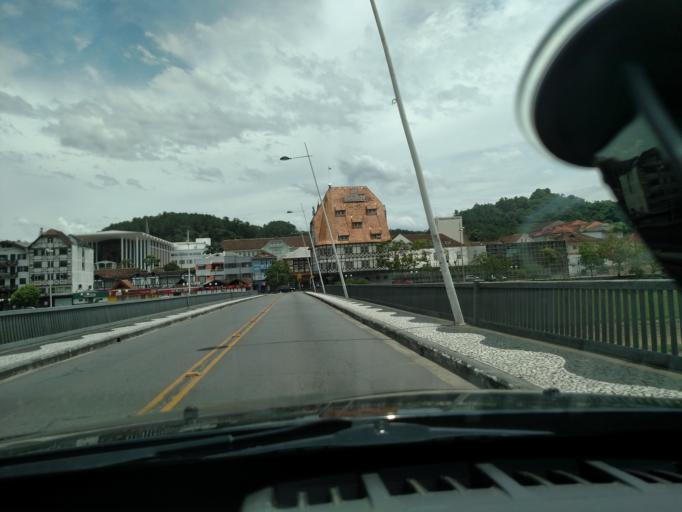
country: BR
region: Santa Catarina
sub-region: Blumenau
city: Blumenau
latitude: -26.9180
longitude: -49.0651
